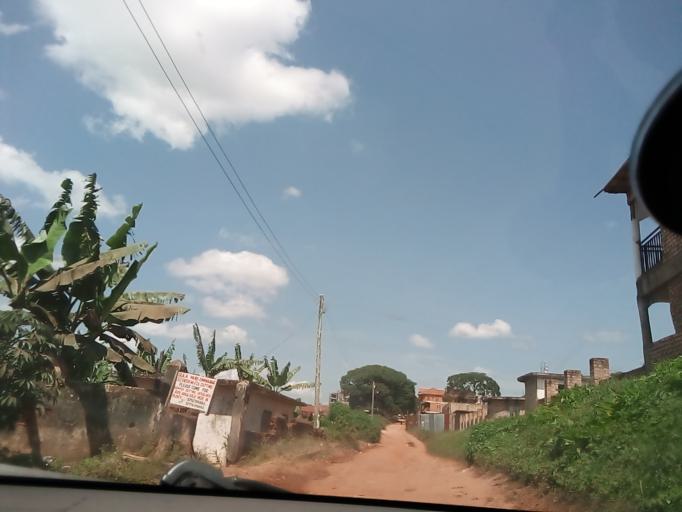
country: UG
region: Central Region
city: Masaka
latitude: -0.3373
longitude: 31.7417
